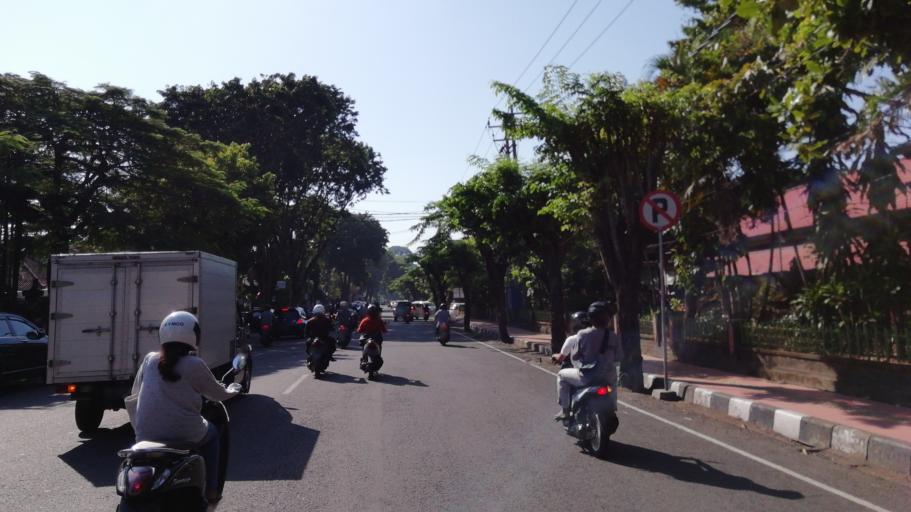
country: ID
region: Bali
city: Denpasar
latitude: -8.6564
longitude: 115.2193
